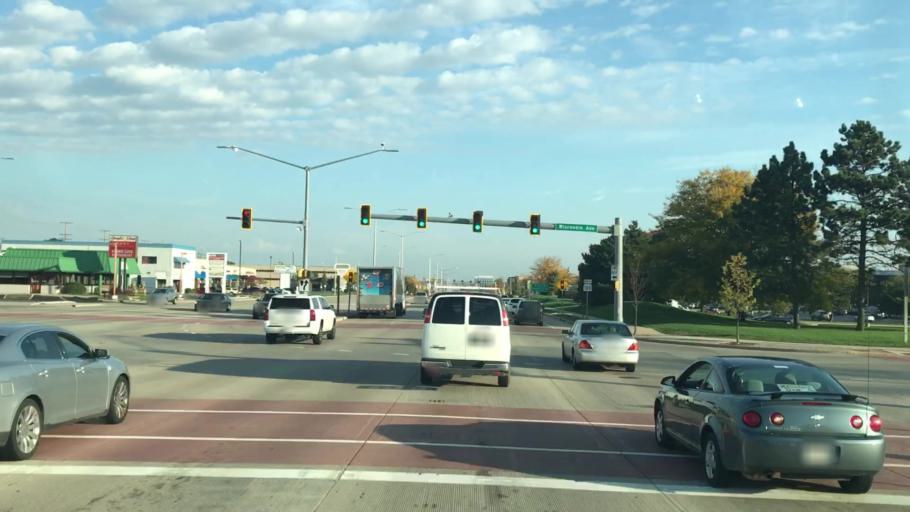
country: US
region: Wisconsin
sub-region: Waukesha County
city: Elm Grove
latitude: 43.0381
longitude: -88.0470
